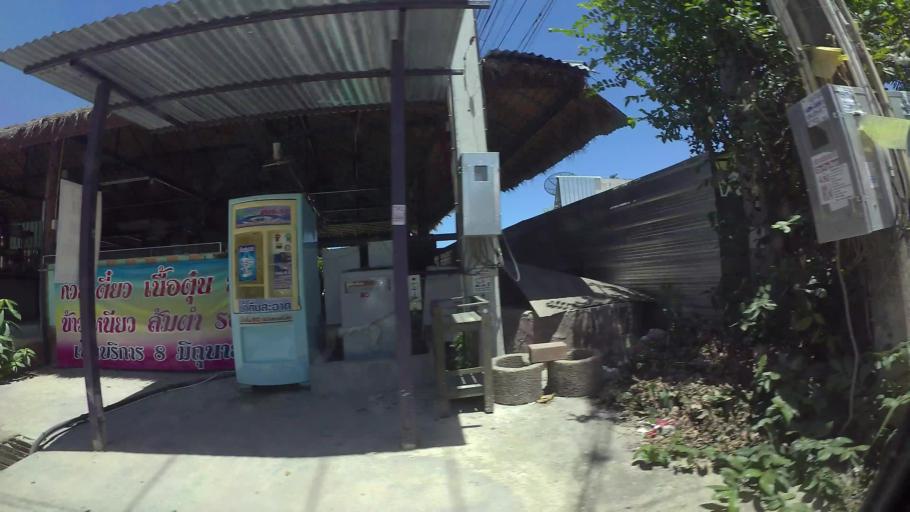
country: TH
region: Chon Buri
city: Phatthaya
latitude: 12.9220
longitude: 100.8920
